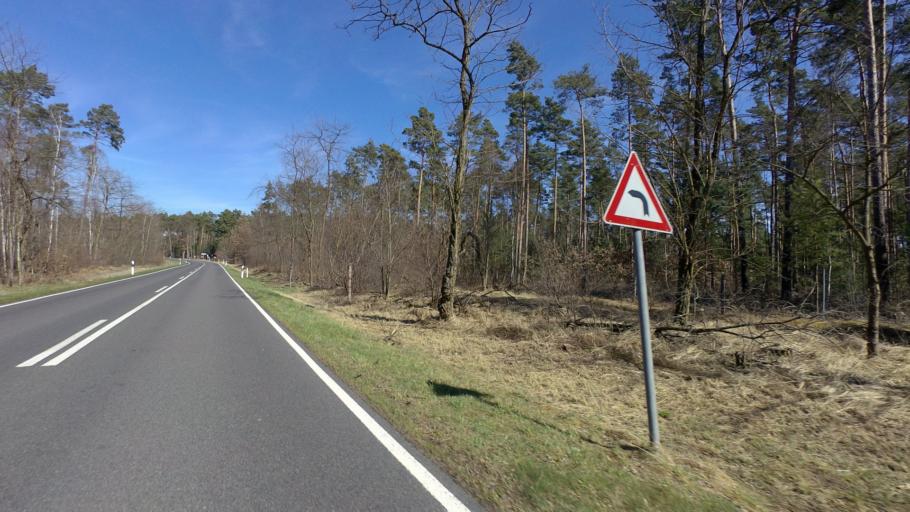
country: DE
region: Brandenburg
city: Storkow
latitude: 52.2184
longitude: 13.9470
